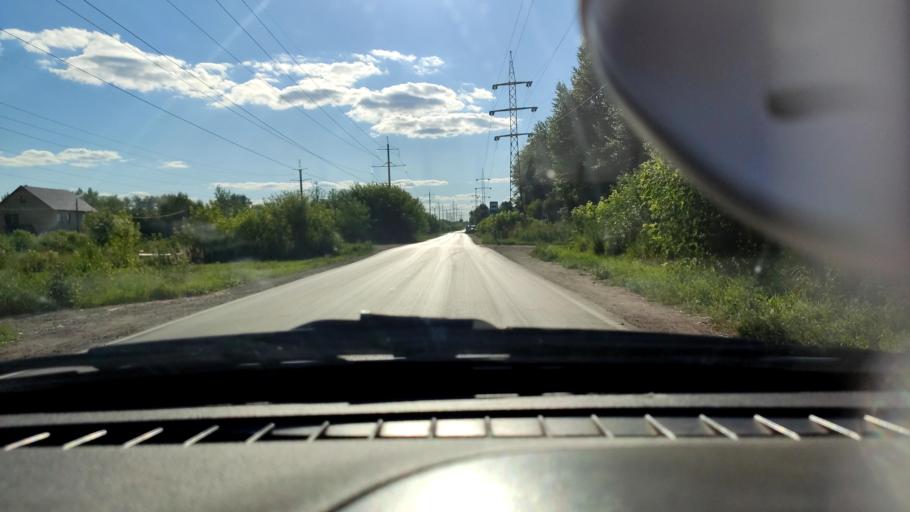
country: RU
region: Perm
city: Krasnokamsk
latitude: 58.0744
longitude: 55.8008
